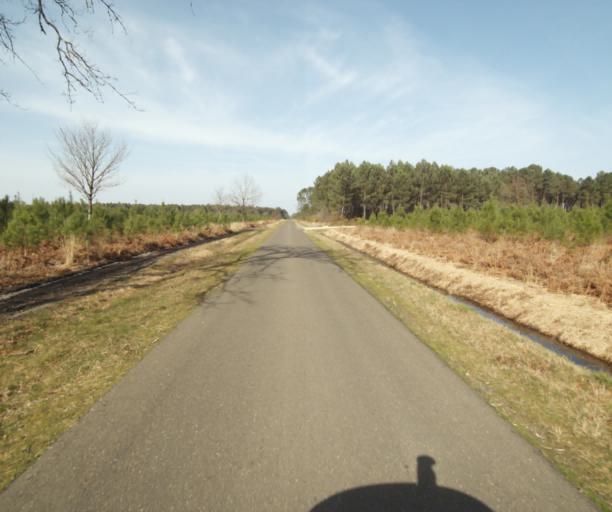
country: FR
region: Aquitaine
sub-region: Departement des Landes
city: Roquefort
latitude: 44.1983
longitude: -0.1963
